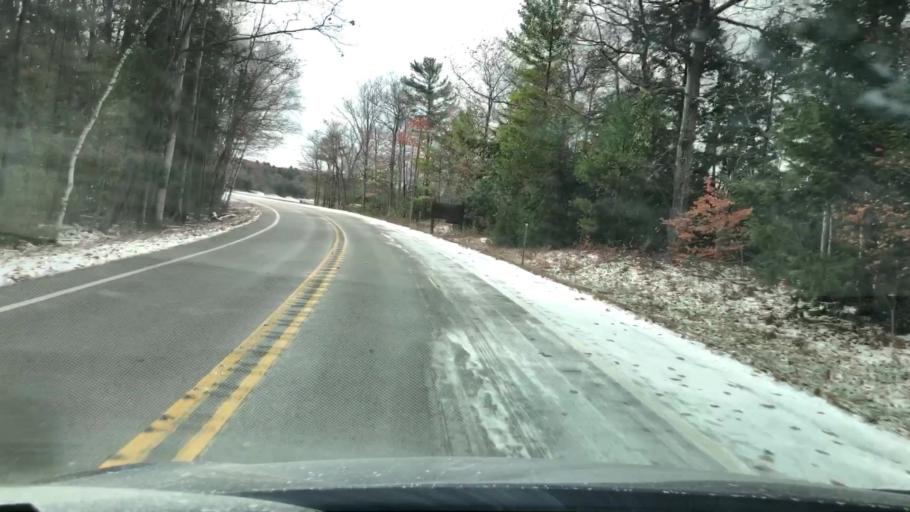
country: US
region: Michigan
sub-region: Antrim County
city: Elk Rapids
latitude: 44.9881
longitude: -85.4940
